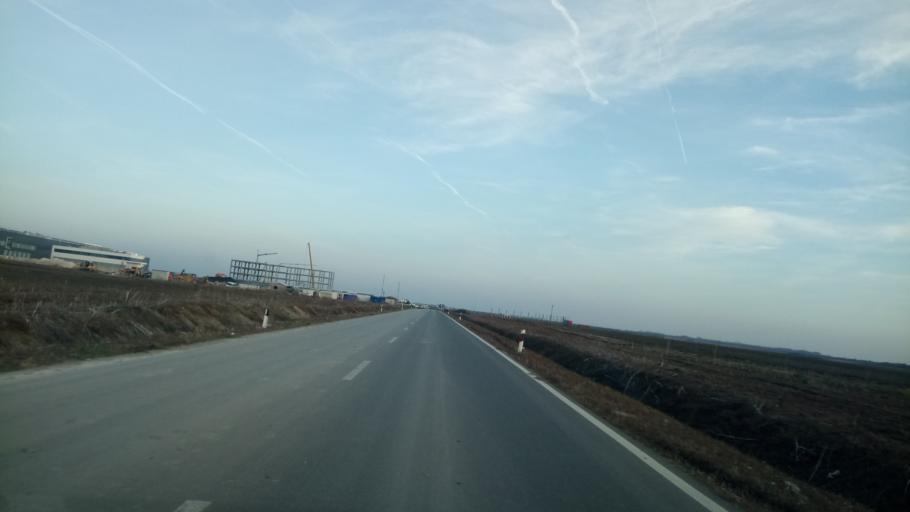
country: RS
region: Autonomna Pokrajina Vojvodina
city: Nova Pazova
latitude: 44.9631
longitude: 20.2345
